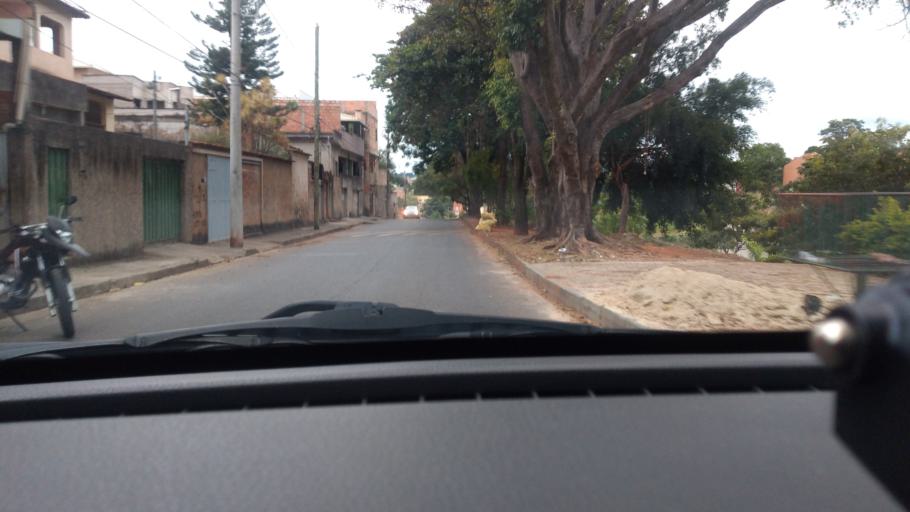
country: BR
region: Minas Gerais
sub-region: Belo Horizonte
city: Belo Horizonte
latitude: -19.8303
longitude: -43.9347
